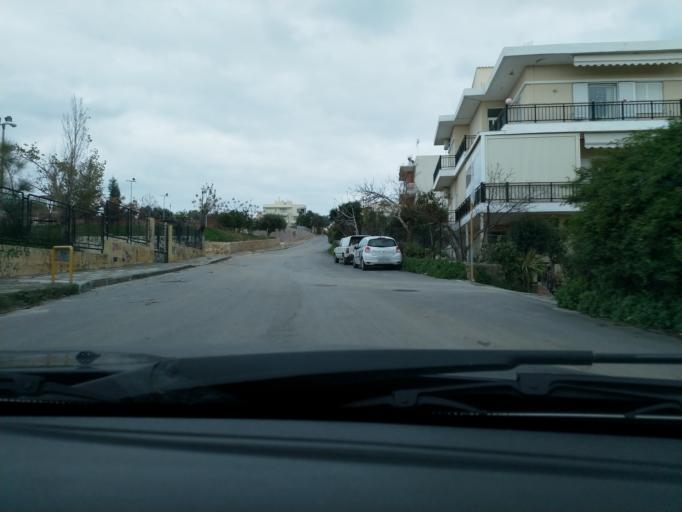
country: GR
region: Crete
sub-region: Nomos Chanias
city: Chania
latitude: 35.5117
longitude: 24.0370
